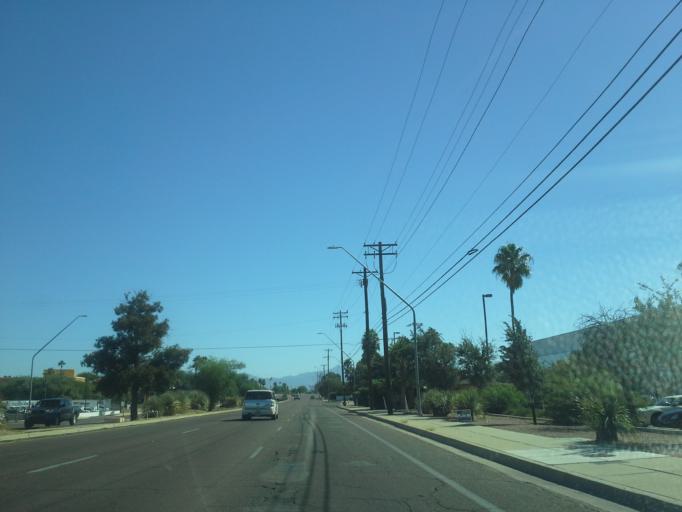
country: US
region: Arizona
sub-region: Pima County
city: Summit
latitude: 32.1340
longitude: -110.9321
